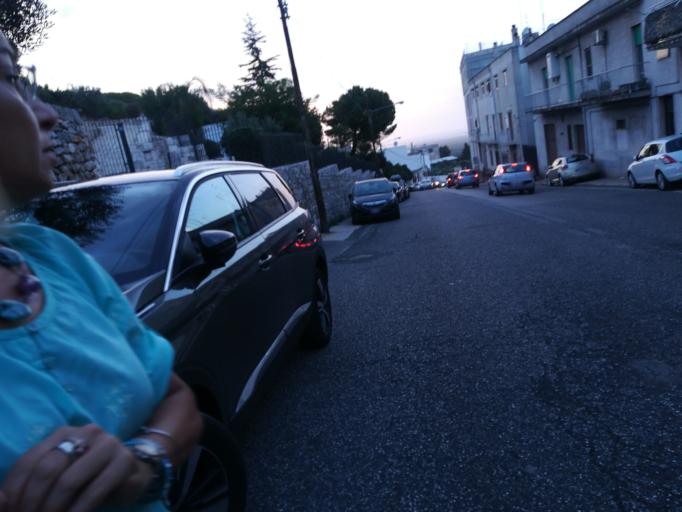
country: IT
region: Apulia
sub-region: Provincia di Brindisi
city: Ostuni
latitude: 40.7308
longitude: 17.5708
